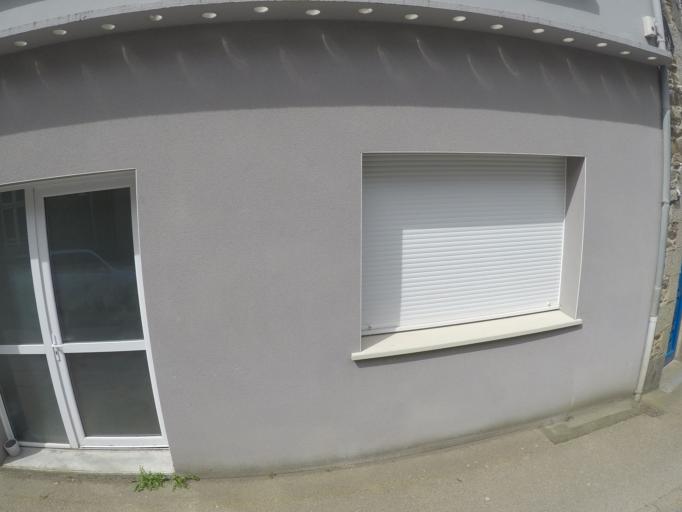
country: FR
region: Brittany
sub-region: Departement des Cotes-d'Armor
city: Plouha
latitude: 48.6771
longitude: -2.9273
